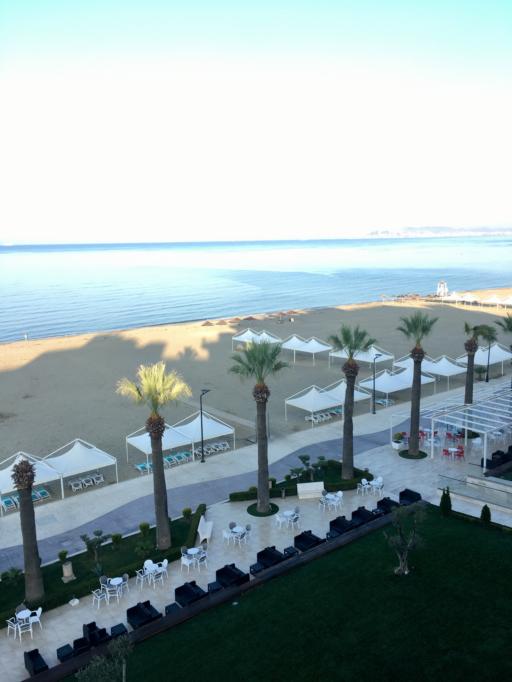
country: AL
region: Tirane
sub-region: Rrethi i Kavajes
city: Golem
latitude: 41.2622
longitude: 19.5202
